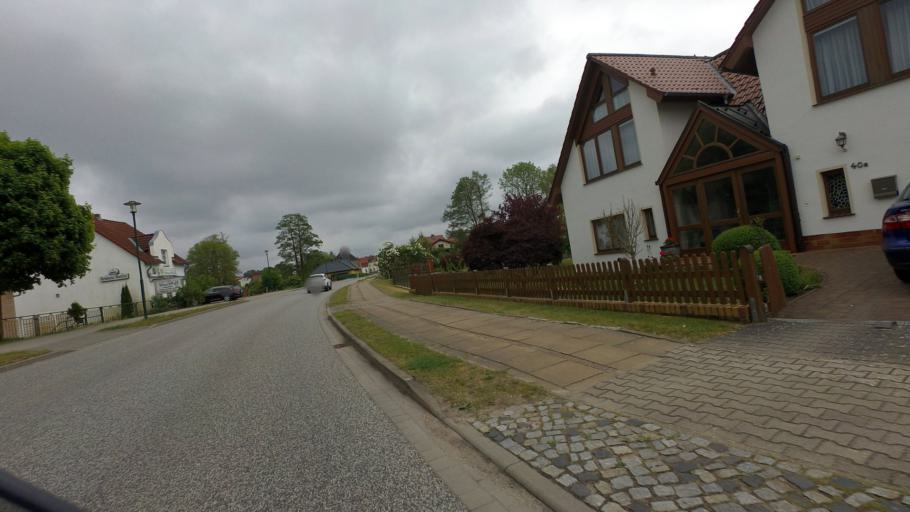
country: DE
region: Brandenburg
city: Lychen
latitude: 53.2125
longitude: 13.3026
